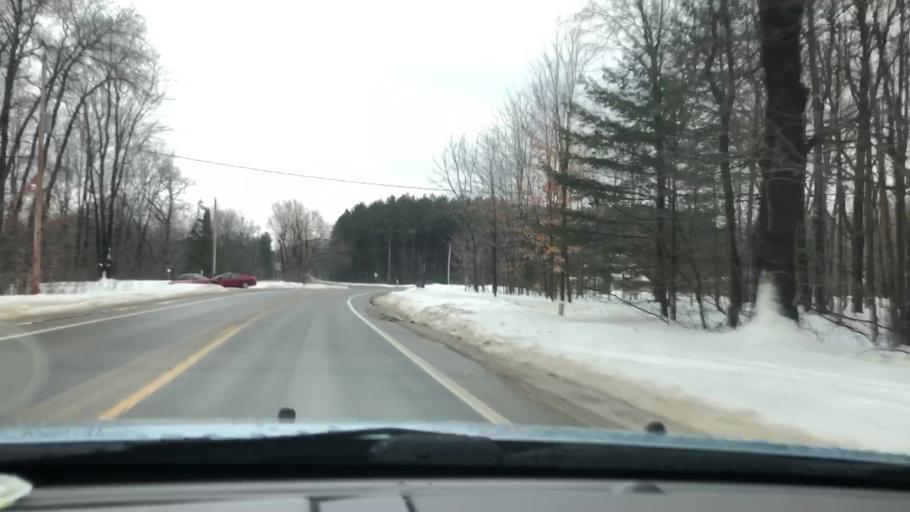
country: US
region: Michigan
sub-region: Charlevoix County
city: East Jordan
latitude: 45.1324
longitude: -85.0949
